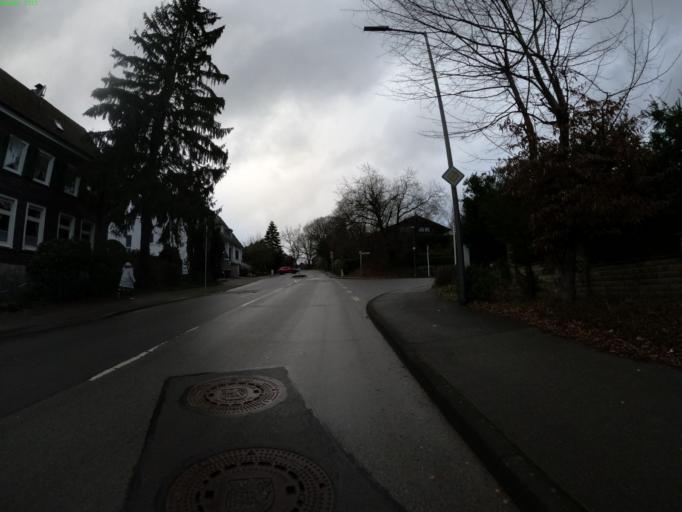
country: DE
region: North Rhine-Westphalia
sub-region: Regierungsbezirk Dusseldorf
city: Solingen
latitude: 51.1893
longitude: 7.1334
